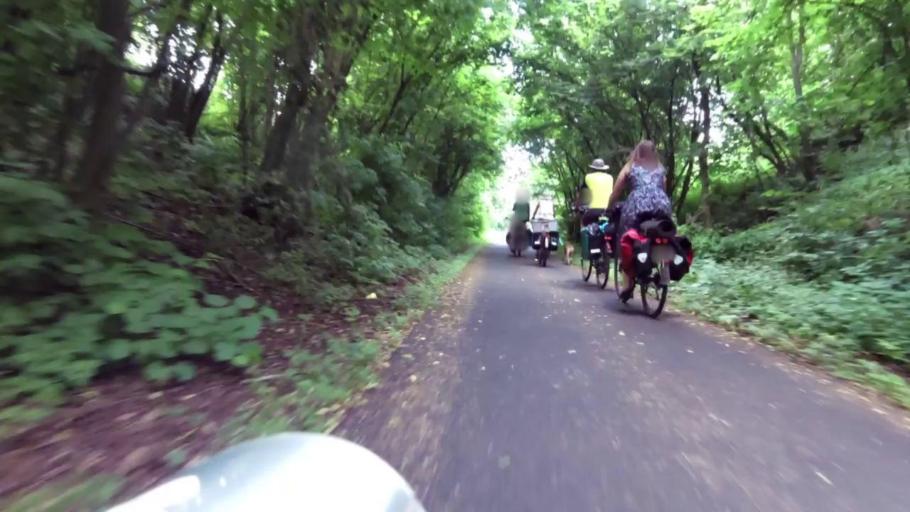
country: PL
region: Kujawsko-Pomorskie
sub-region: Powiat torunski
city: Lubianka
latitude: 53.0908
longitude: 18.5330
